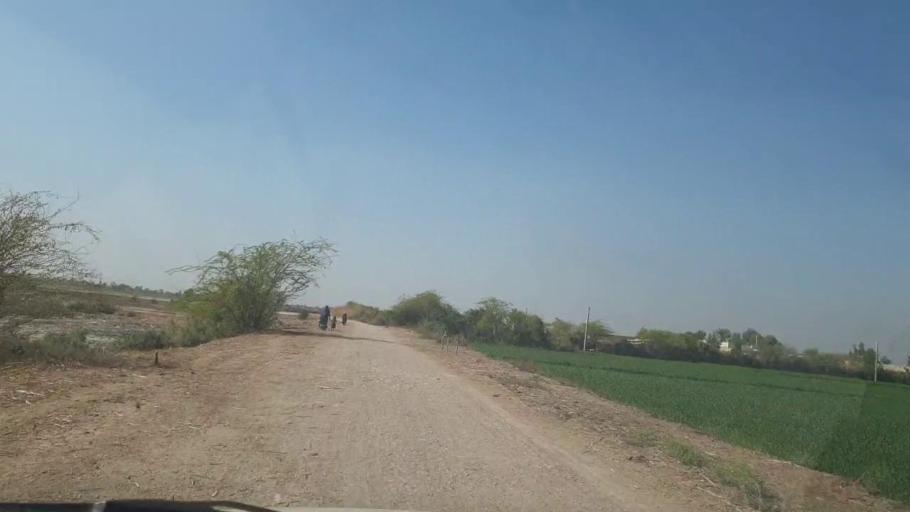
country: PK
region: Sindh
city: Mirpur Khas
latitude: 25.4733
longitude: 69.1245
